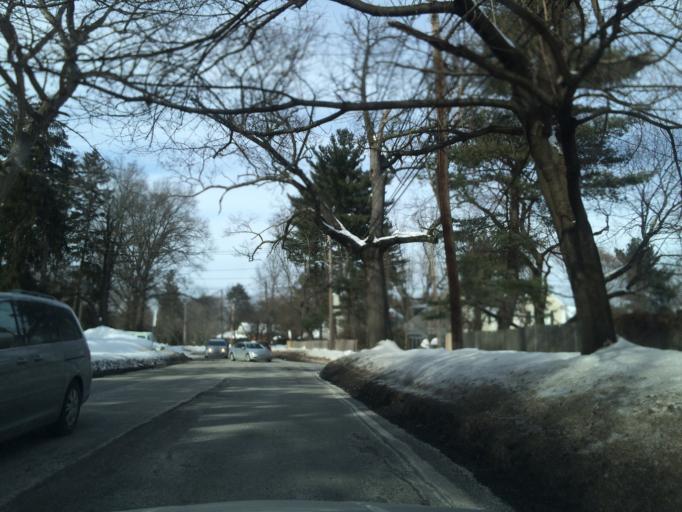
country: US
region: Massachusetts
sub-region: Middlesex County
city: Newton
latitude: 42.3064
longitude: -71.1949
